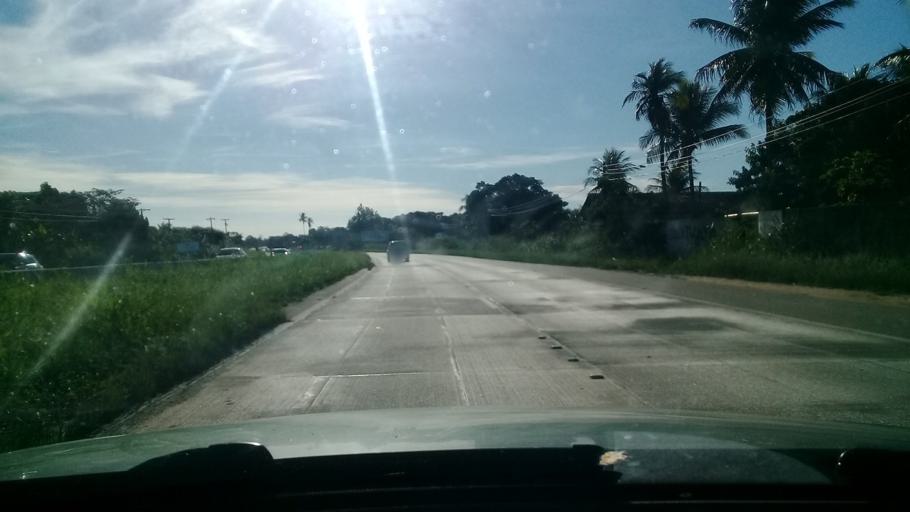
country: BR
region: Pernambuco
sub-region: Carpina
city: Carpina
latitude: -7.8723
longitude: -35.1916
